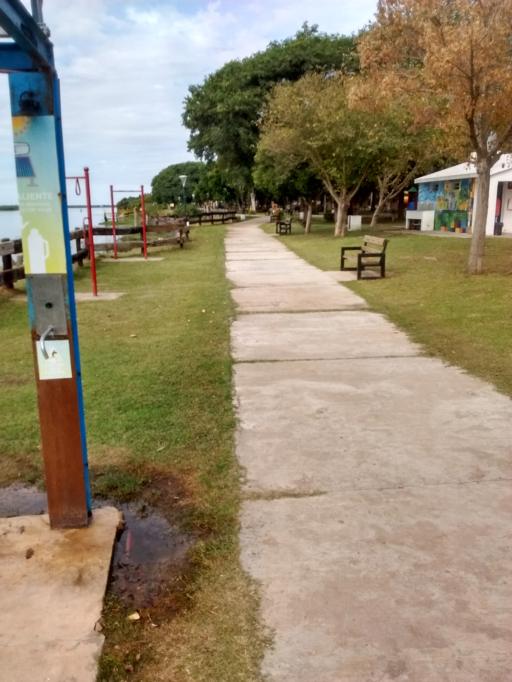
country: AR
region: Santa Fe
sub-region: Departamento de San Lorenzo
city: San Lorenzo
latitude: -32.4316
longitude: -60.8125
